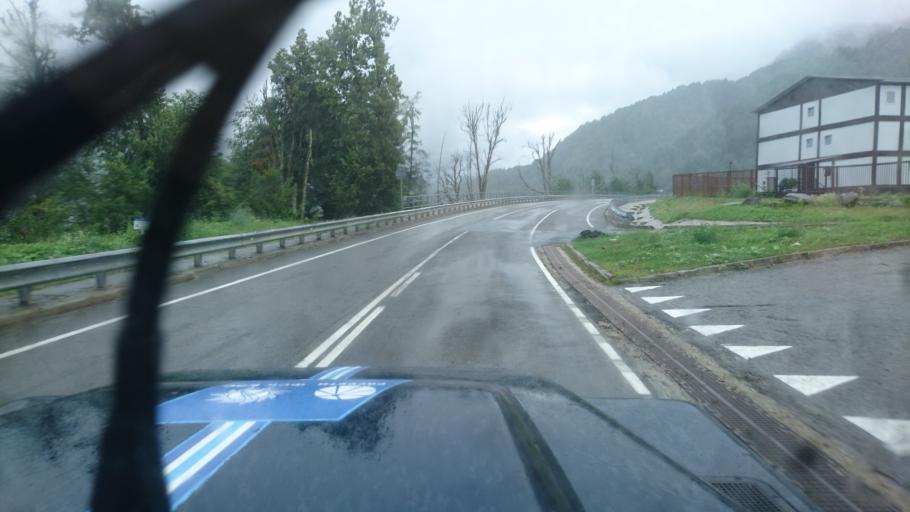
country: RU
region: Krasnodarskiy
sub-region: Sochi City
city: Krasnaya Polyana
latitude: 43.6483
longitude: 40.3394
